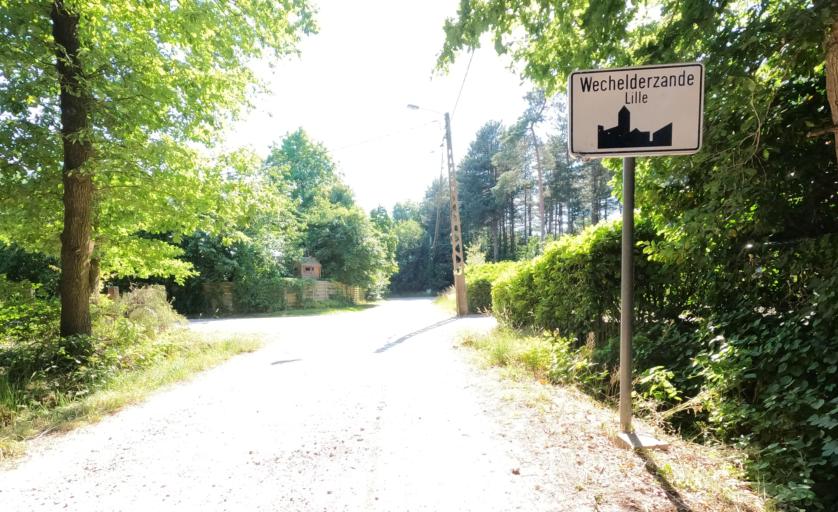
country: BE
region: Flanders
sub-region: Provincie Antwerpen
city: Lille
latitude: 51.2721
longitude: 4.7896
